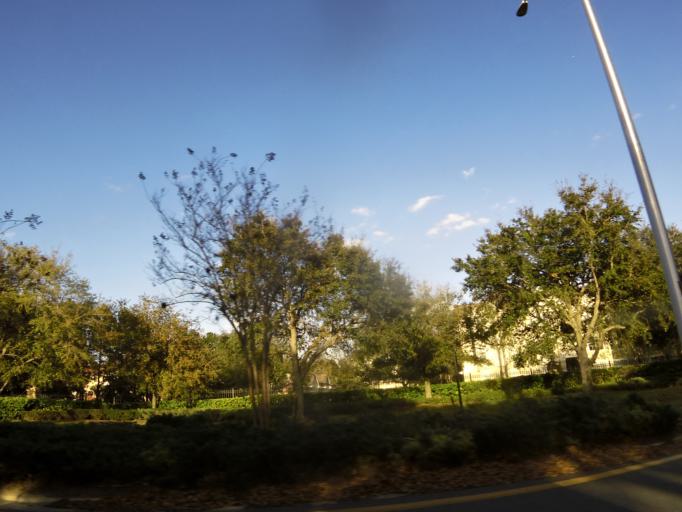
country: US
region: Florida
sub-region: Duval County
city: Jacksonville
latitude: 30.2670
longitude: -81.5508
